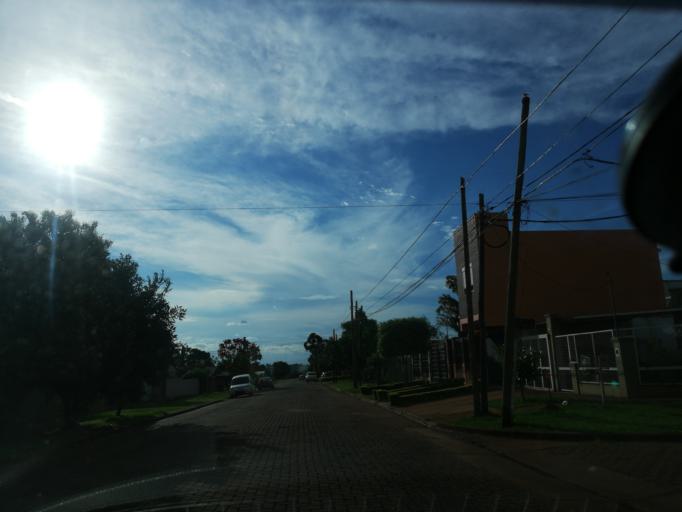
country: AR
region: Misiones
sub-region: Departamento de Capital
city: Posadas
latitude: -27.4206
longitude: -55.9512
